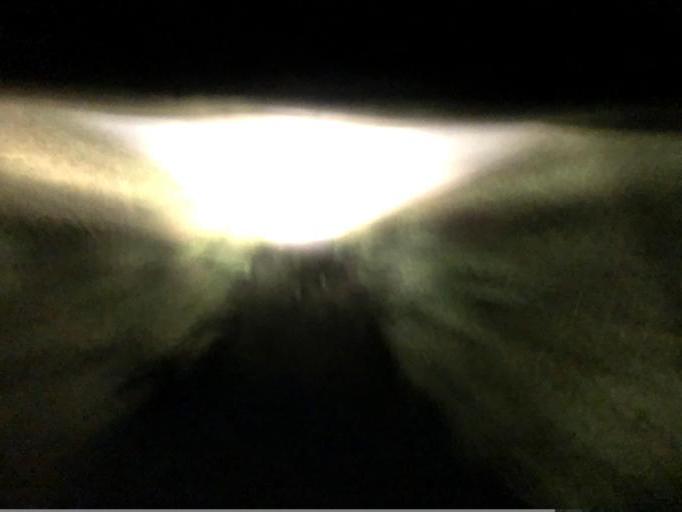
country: TH
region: Nakhon Sawan
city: Takhli
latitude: 15.2542
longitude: 100.3341
